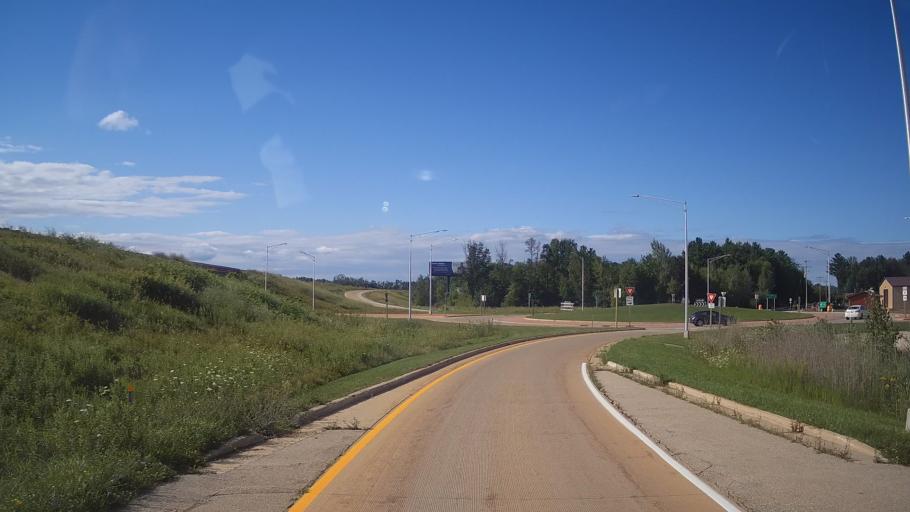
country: US
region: Wisconsin
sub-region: Oconto County
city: Oconto
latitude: 44.8911
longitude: -87.8955
